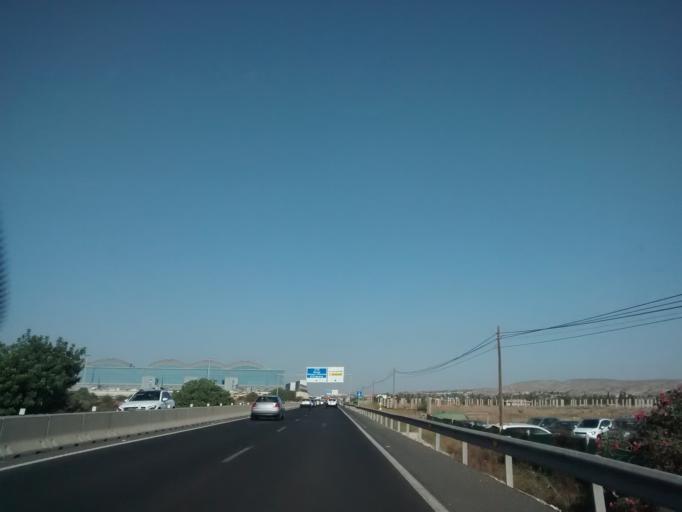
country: ES
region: Valencia
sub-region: Provincia de Alicante
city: Alicante
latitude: 38.2867
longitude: -0.5436
